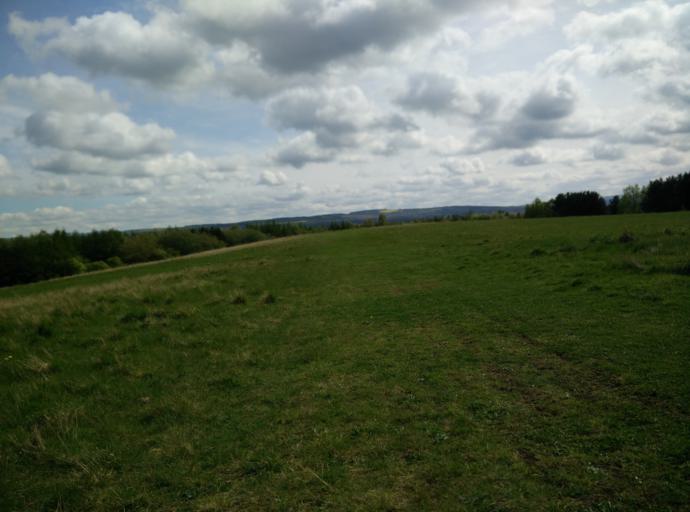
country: GB
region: Scotland
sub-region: Midlothian
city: Dalkeith
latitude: 55.9175
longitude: -3.1030
